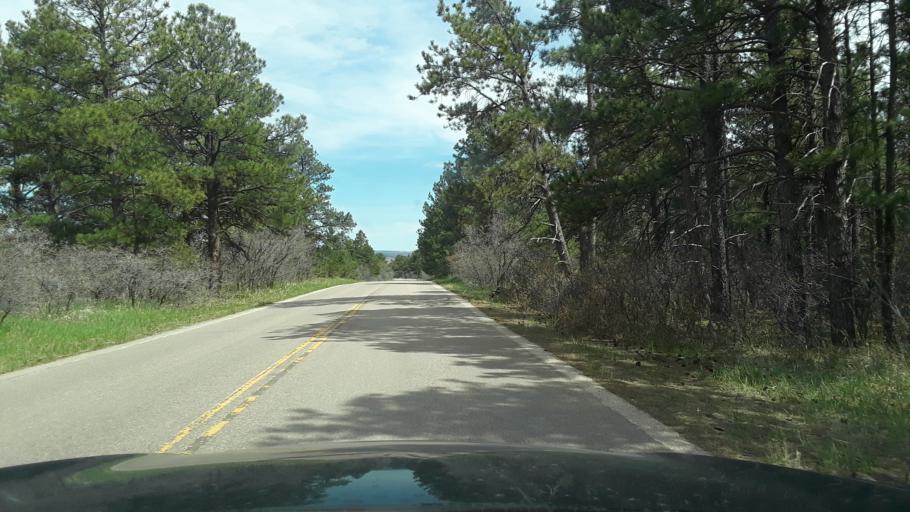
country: US
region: Colorado
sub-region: El Paso County
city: Monument
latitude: 39.0867
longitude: -104.8920
